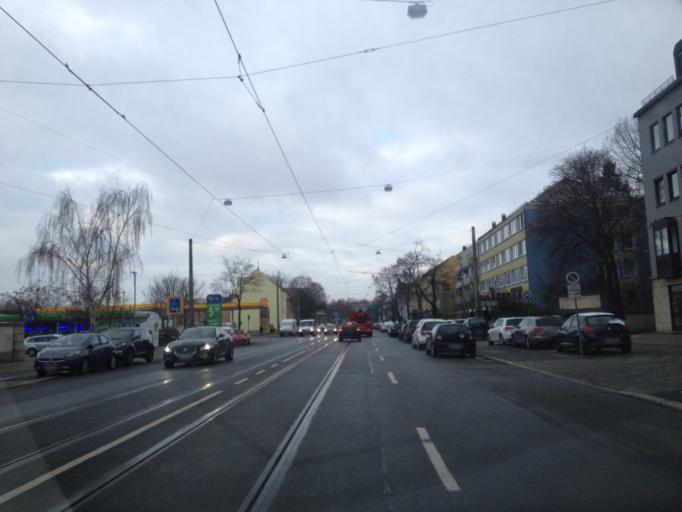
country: DE
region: Bavaria
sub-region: Regierungsbezirk Mittelfranken
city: Nuernberg
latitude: 49.4665
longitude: 11.1237
